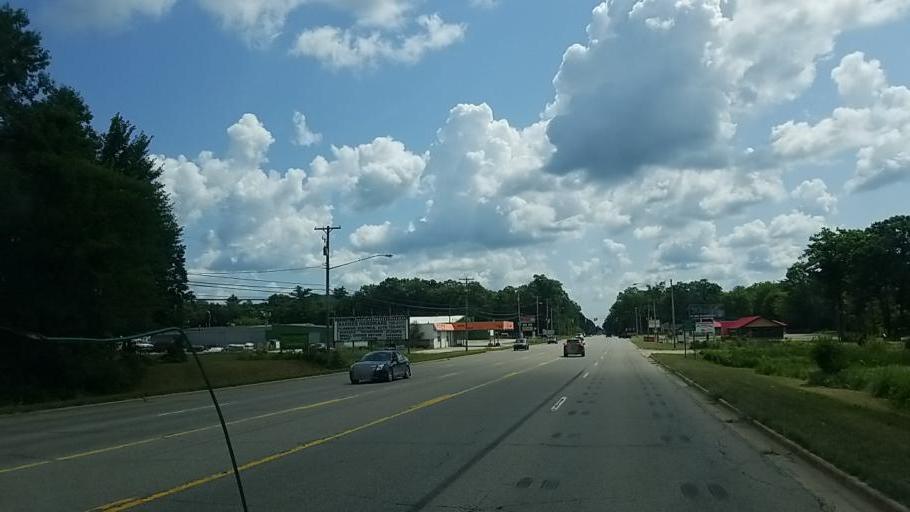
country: US
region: Michigan
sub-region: Muskegon County
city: Wolf Lake
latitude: 43.2349
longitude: -86.0703
